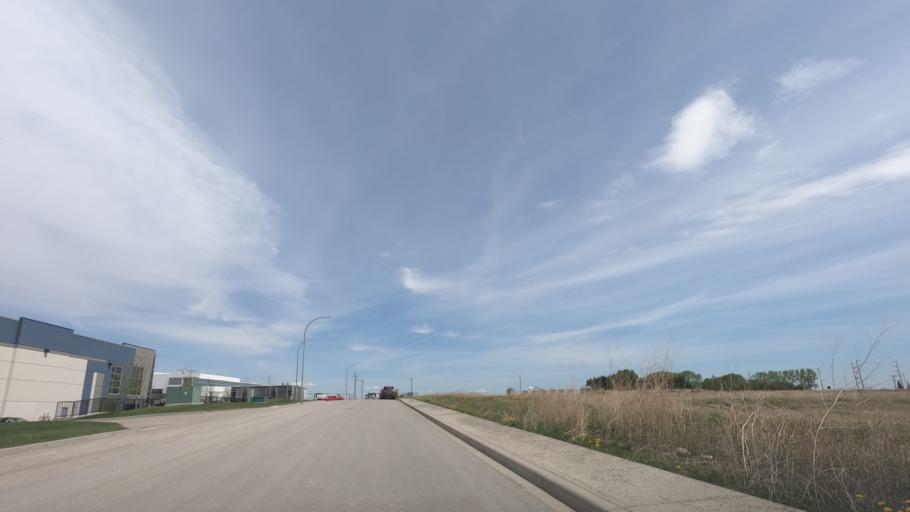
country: CA
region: Alberta
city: Airdrie
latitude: 51.3027
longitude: -113.9824
